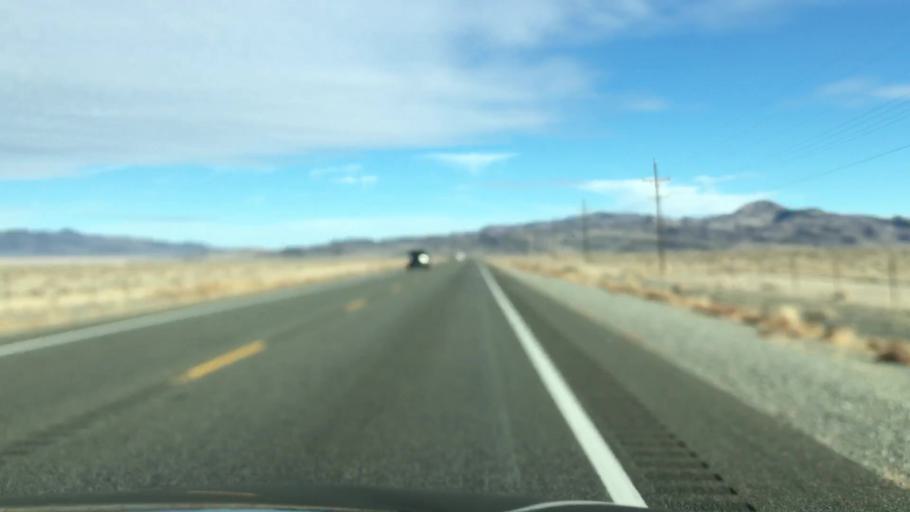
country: US
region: Nevada
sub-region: Mineral County
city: Hawthorne
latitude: 38.5245
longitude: -118.5845
